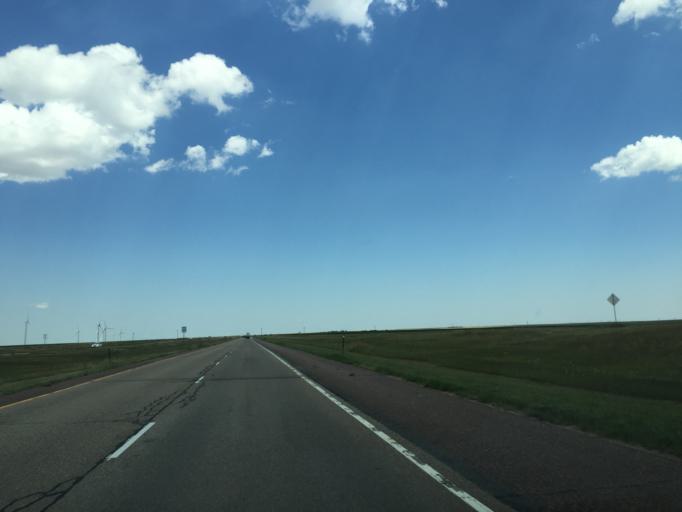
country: US
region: Colorado
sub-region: Lincoln County
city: Hugo
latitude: 39.2780
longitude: -103.4332
